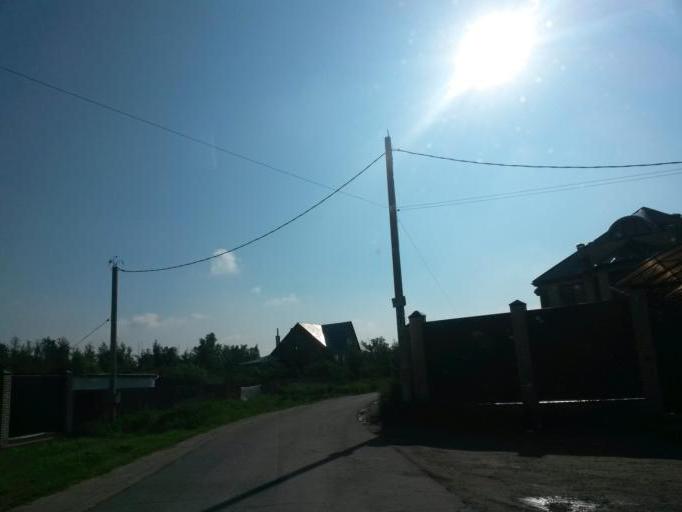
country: RU
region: Moscow
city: Zyablikovo
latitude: 55.5912
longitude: 37.7829
